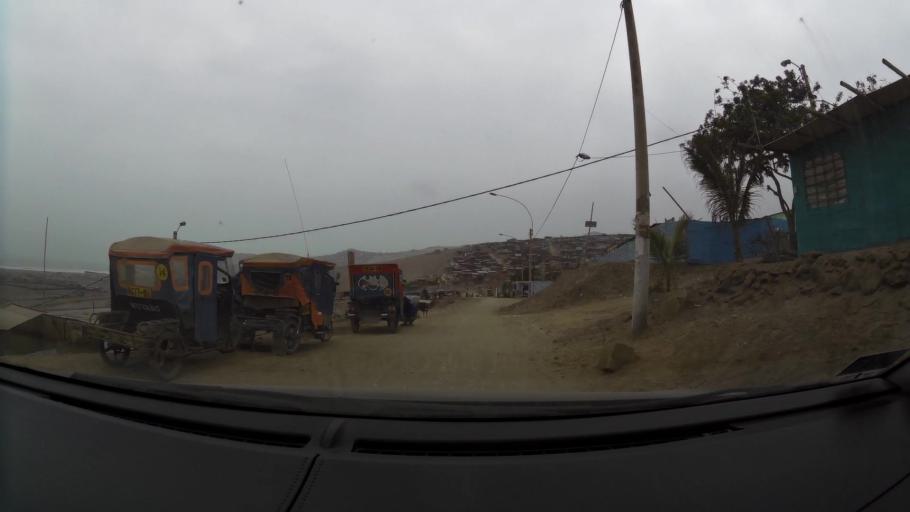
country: PE
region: Lima
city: Ventanilla
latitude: -11.8477
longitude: -77.1585
